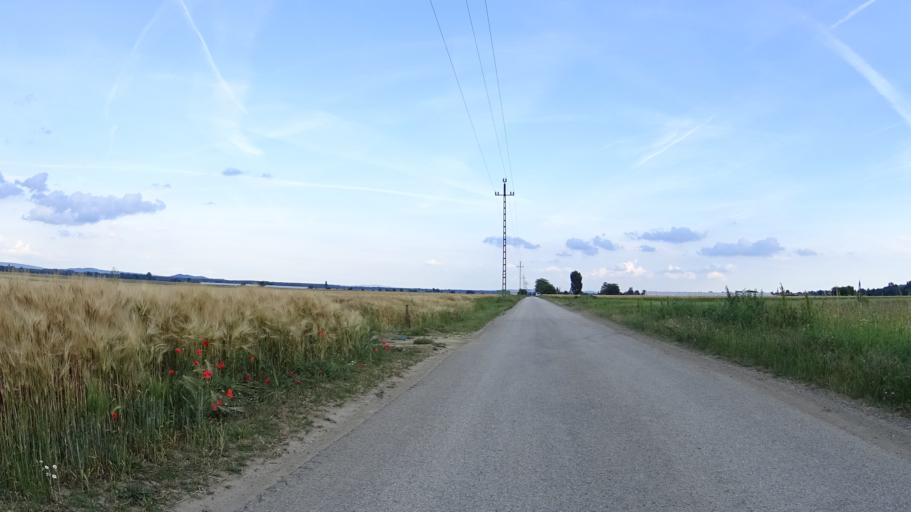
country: HU
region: Pest
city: Tahitotfalu
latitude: 47.7665
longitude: 19.0875
